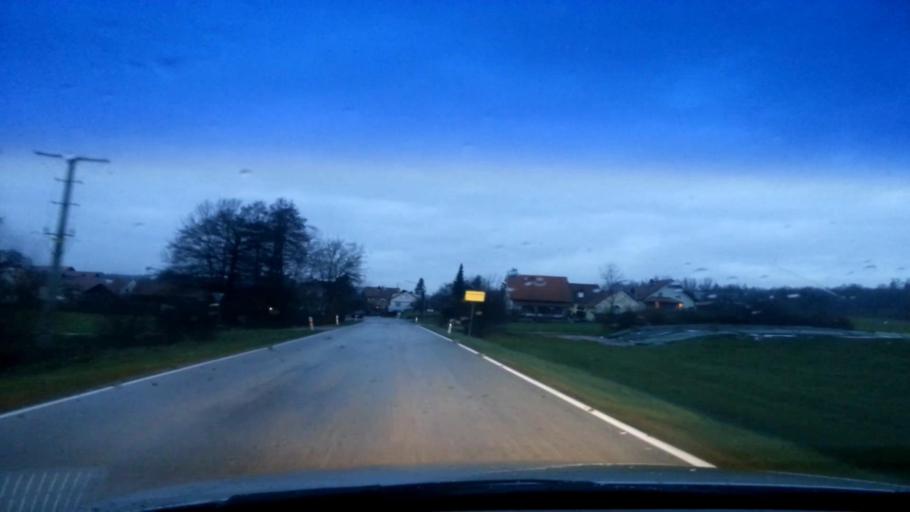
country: DE
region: Bavaria
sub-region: Upper Franconia
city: Schesslitz
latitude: 49.9716
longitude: 10.9880
